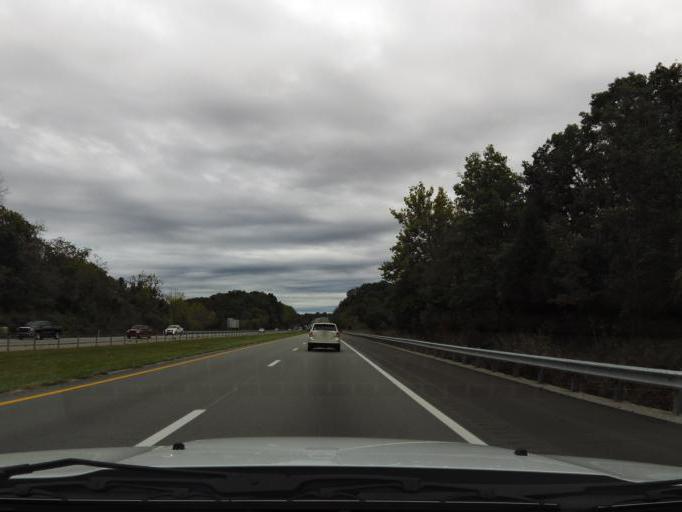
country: US
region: Kentucky
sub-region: Rockcastle County
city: Mount Vernon
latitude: 37.4114
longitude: -84.3402
